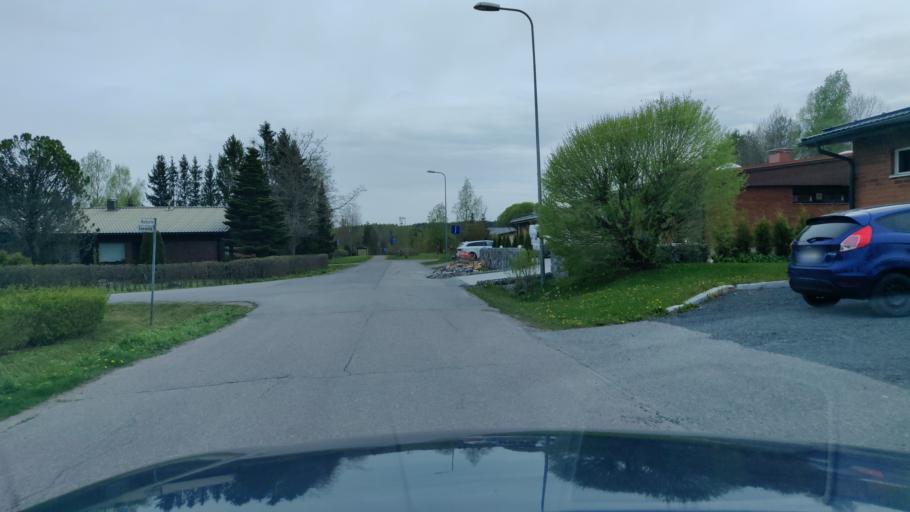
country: FI
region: Uusimaa
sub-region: Helsinki
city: Nurmijaervi
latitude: 60.3671
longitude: 24.7445
